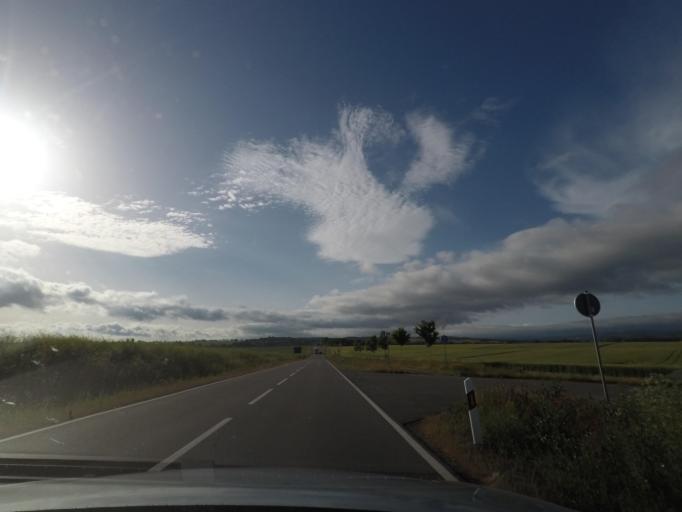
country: DE
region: Saxony-Anhalt
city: Derenburg
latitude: 51.8795
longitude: 10.8958
